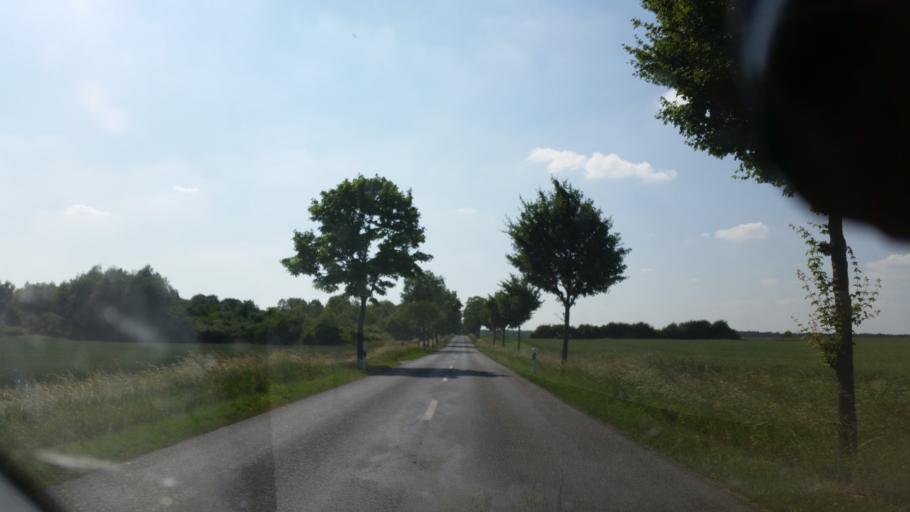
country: DE
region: Lower Saxony
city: Lehre
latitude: 52.3136
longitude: 10.7518
